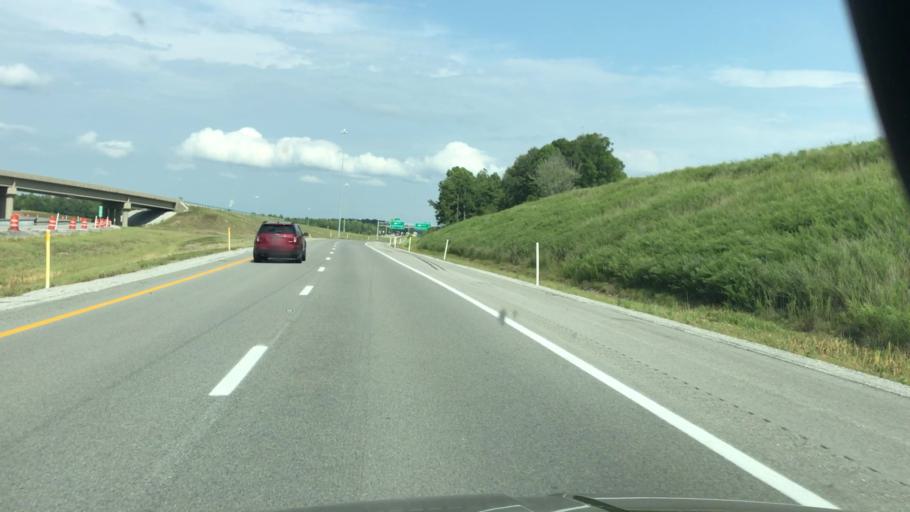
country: US
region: Kentucky
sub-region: Hopkins County
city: Nortonville
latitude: 37.2123
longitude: -87.4506
